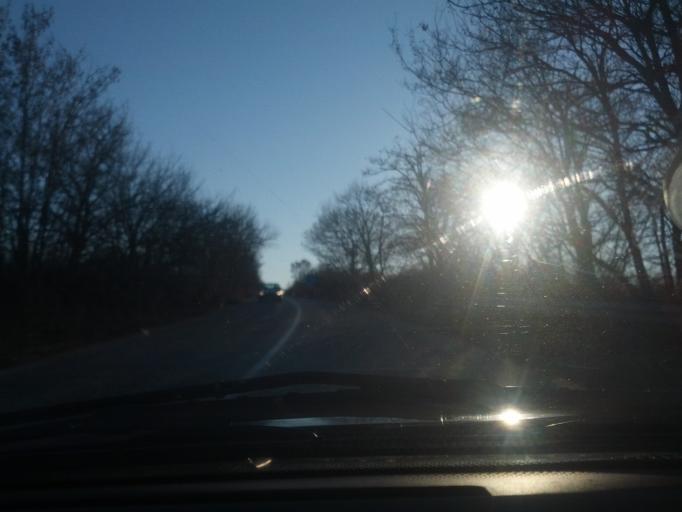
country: BG
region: Vratsa
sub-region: Obshtina Borovan
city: Borovan
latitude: 43.3698
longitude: 23.7015
